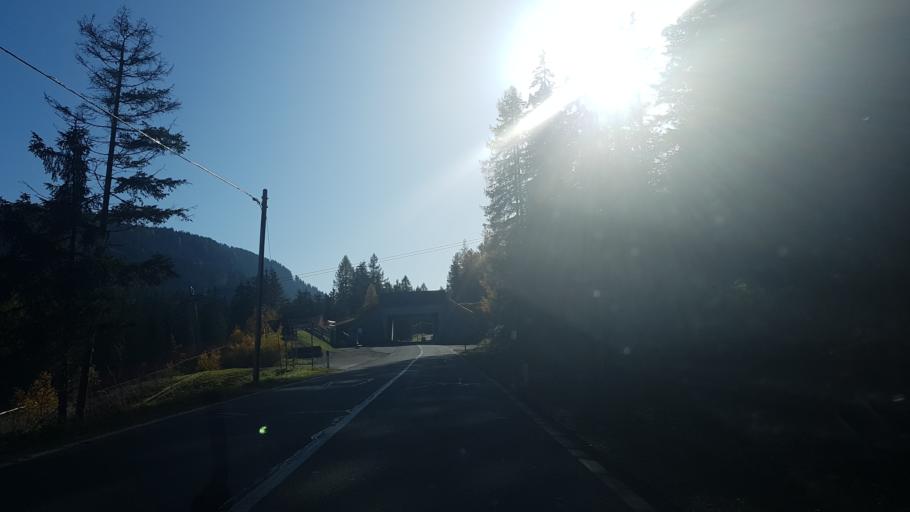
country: IT
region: Trentino-Alto Adige
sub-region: Bolzano
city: Sesto
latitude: 46.6798
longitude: 12.3787
